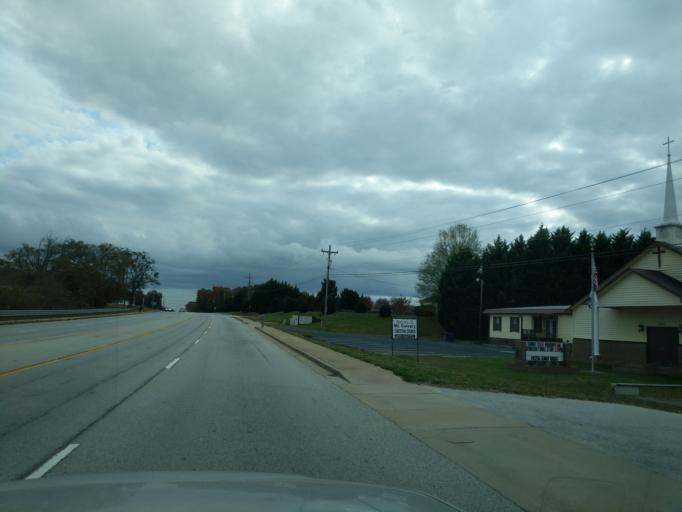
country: US
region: South Carolina
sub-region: Spartanburg County
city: Wellford
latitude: 34.8806
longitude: -82.0569
